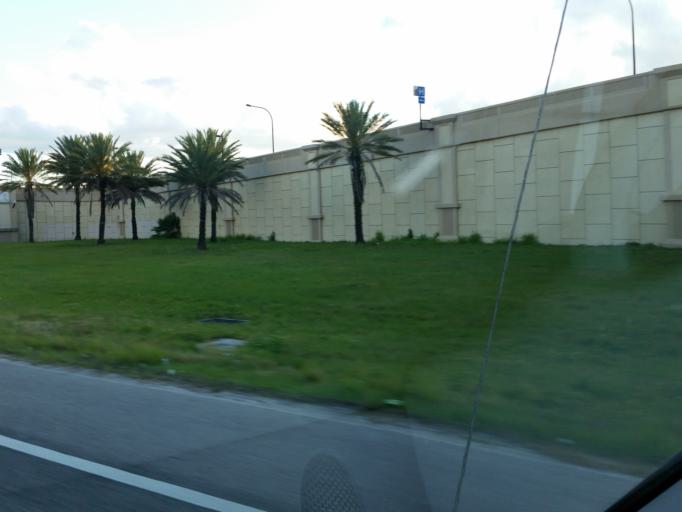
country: US
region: Florida
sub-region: Orange County
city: Orlando
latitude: 28.5371
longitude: -81.3830
